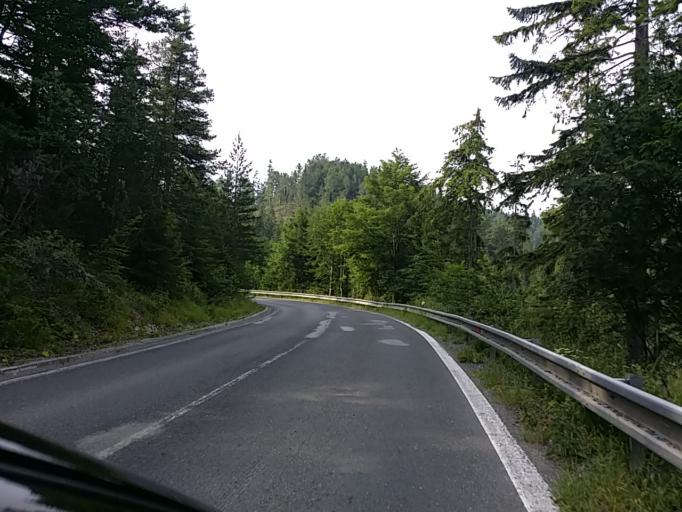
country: SK
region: Kosicky
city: Dobsina
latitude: 48.9026
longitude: 20.2503
